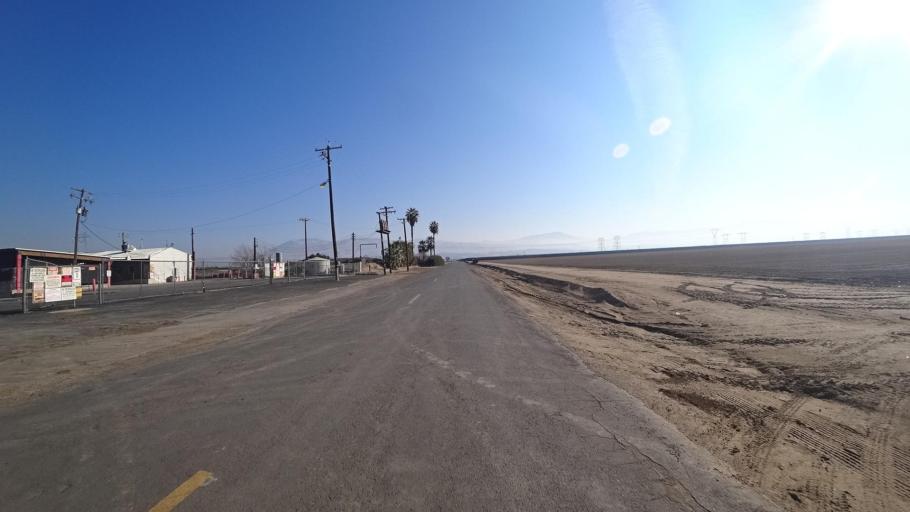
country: US
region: California
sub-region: Kern County
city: Arvin
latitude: 35.1218
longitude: -118.9009
